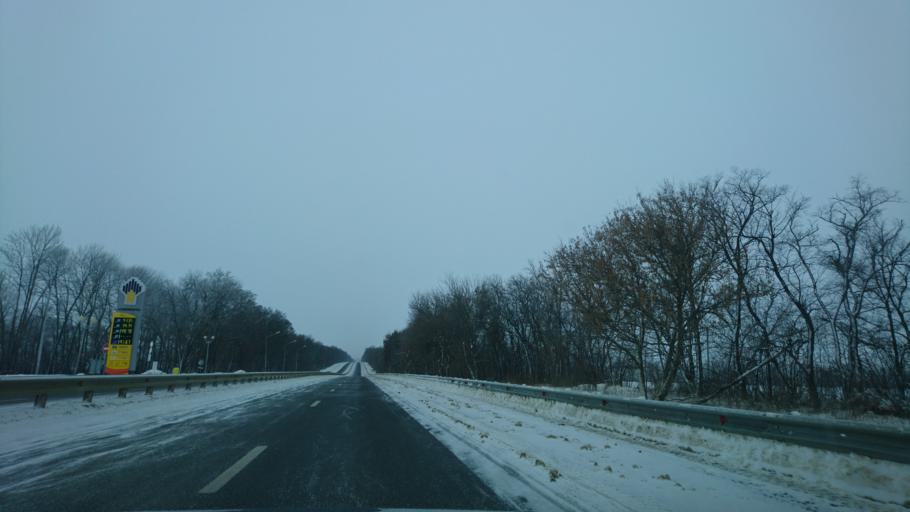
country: RU
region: Belgorod
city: Bessonovka
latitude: 50.3682
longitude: 36.3198
